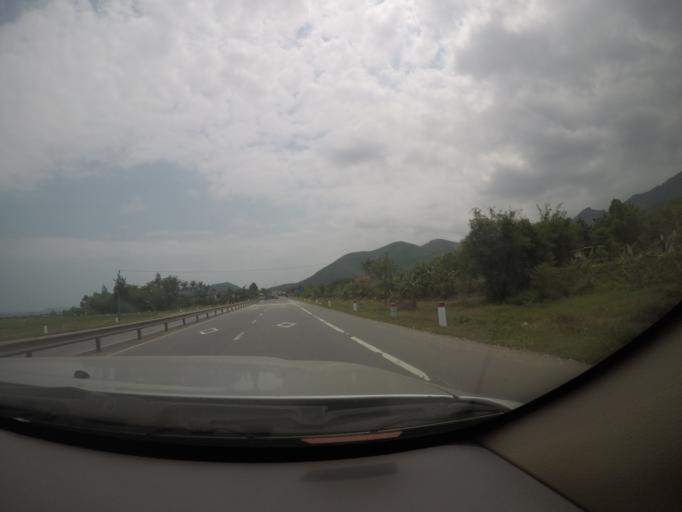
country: VN
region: Thua Thien-Hue
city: Phu Loc
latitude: 16.2881
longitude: 107.8346
